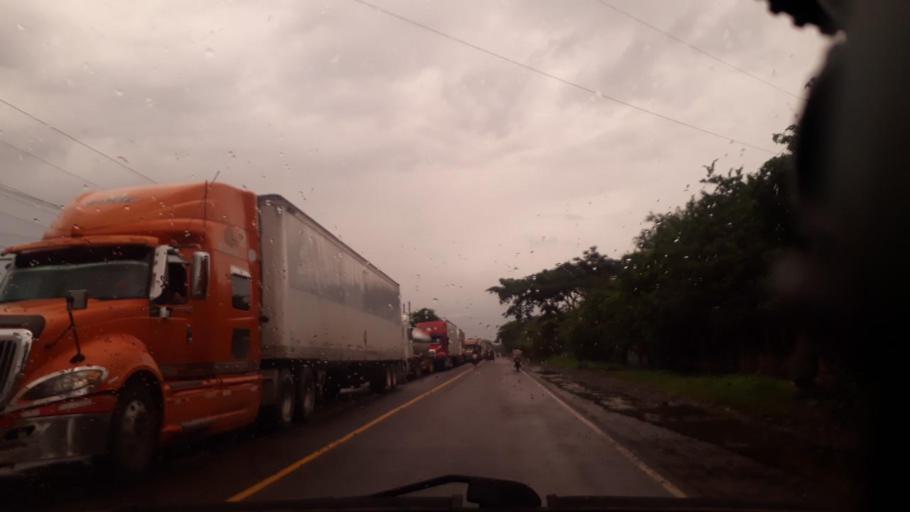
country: SV
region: Ahuachapan
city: San Francisco Menendez
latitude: 13.8805
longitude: -90.1037
